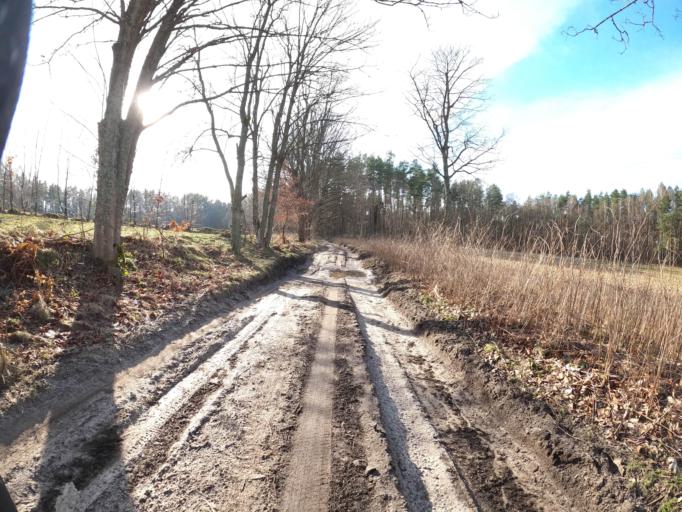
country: PL
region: West Pomeranian Voivodeship
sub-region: Powiat koszalinski
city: Polanow
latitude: 54.2334
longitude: 16.6406
